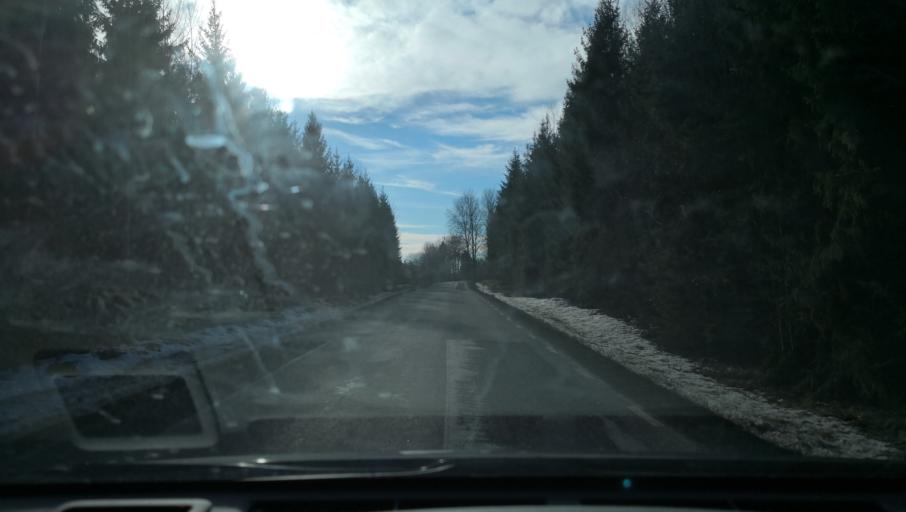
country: SE
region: Uppsala
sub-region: Osthammars Kommun
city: Osterbybruk
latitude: 60.2424
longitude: 17.9301
